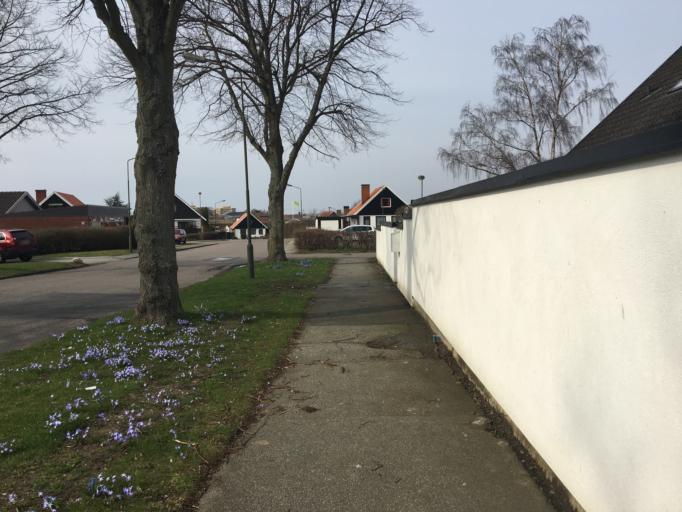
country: SE
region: Skane
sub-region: Burlovs Kommun
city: Arloev
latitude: 55.6373
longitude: 13.0800
